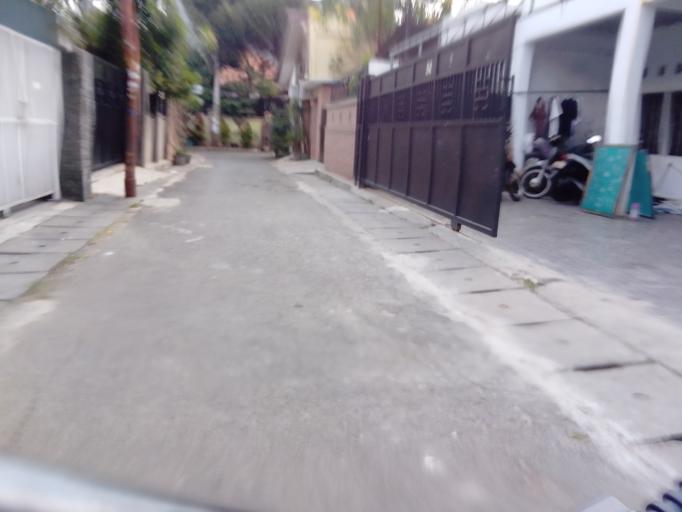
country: ID
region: Jakarta Raya
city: Jakarta
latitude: -6.2071
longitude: 106.8060
